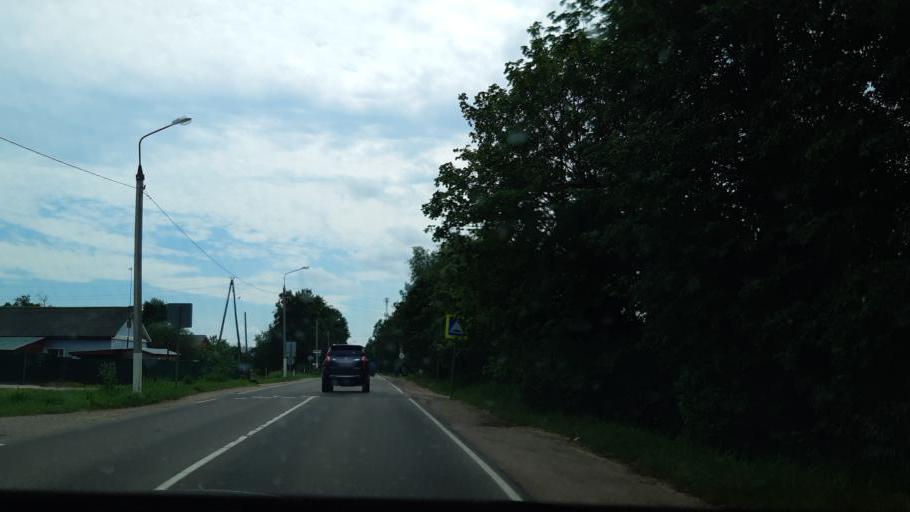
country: RU
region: Moskovskaya
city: Dorokhovo
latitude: 55.4278
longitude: 36.3506
